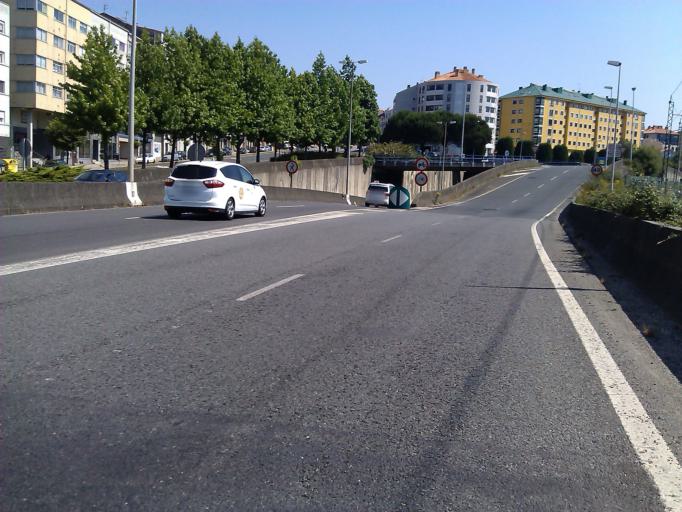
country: ES
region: Galicia
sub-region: Provincia da Coruna
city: Santiago de Compostela
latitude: 42.8771
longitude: -8.5341
